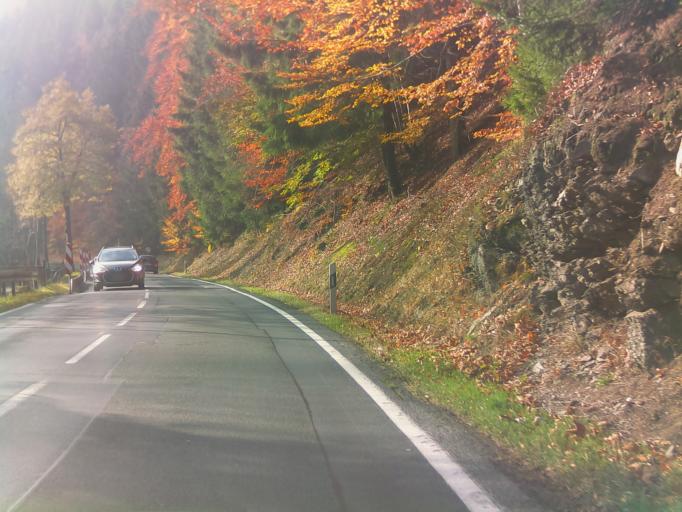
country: DE
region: Thuringia
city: Steinach
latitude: 50.4485
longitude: 11.1454
